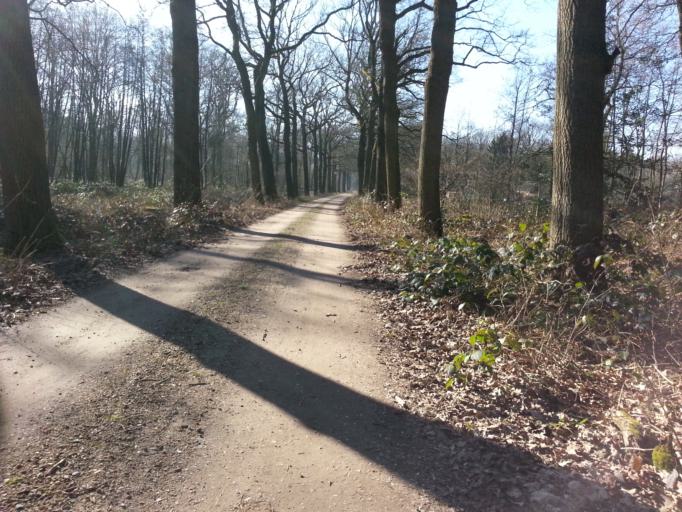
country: NL
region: Utrecht
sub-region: Gemeente Woudenberg
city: Woudenberg
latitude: 52.0571
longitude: 5.4446
